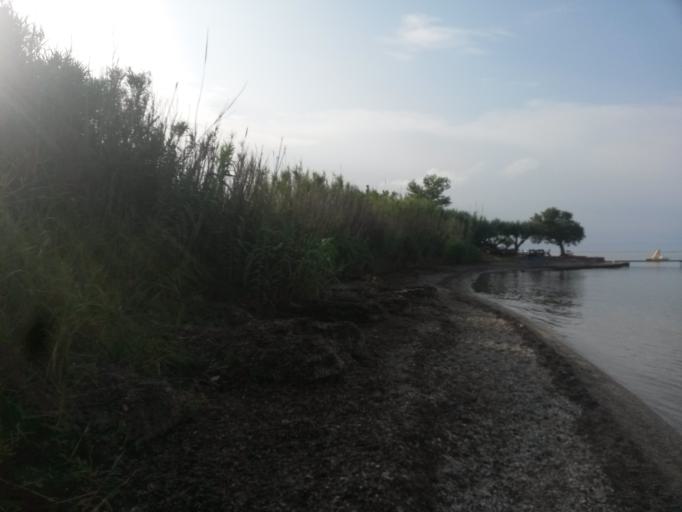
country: GR
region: North Aegean
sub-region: Nomos Lesvou
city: Pamfylla
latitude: 39.1787
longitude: 26.5020
